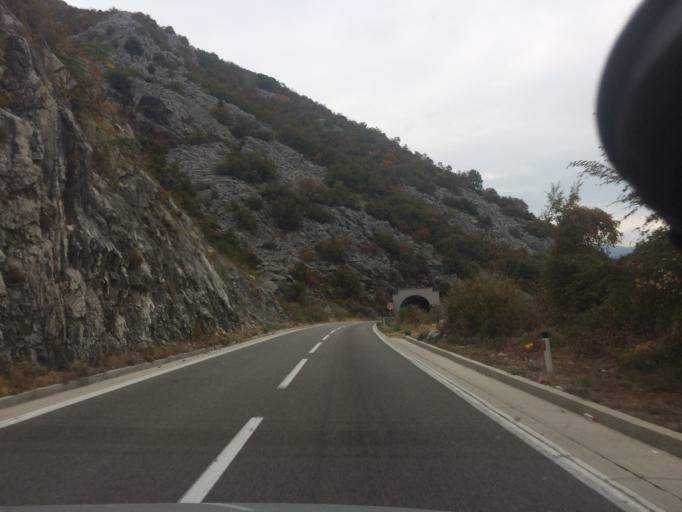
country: ME
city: Lipci
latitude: 42.5012
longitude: 18.6555
